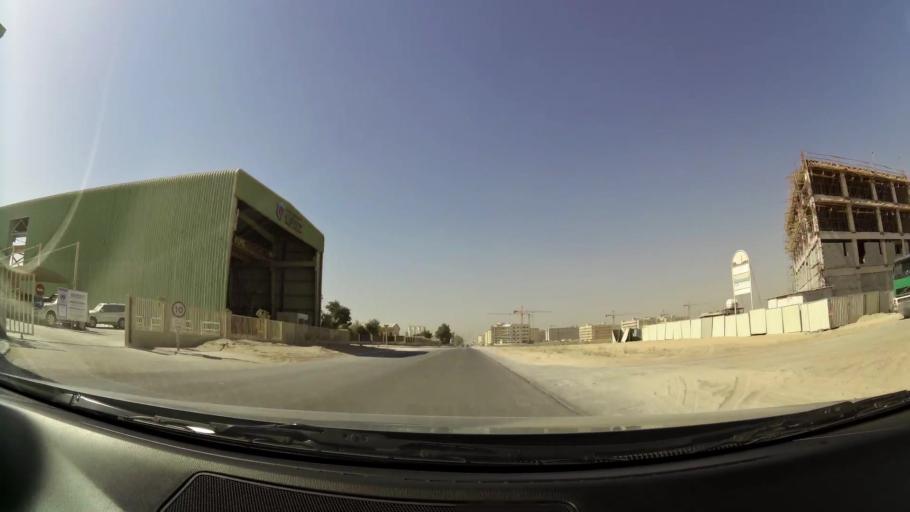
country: AE
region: Dubai
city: Dubai
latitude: 24.9882
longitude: 55.1387
